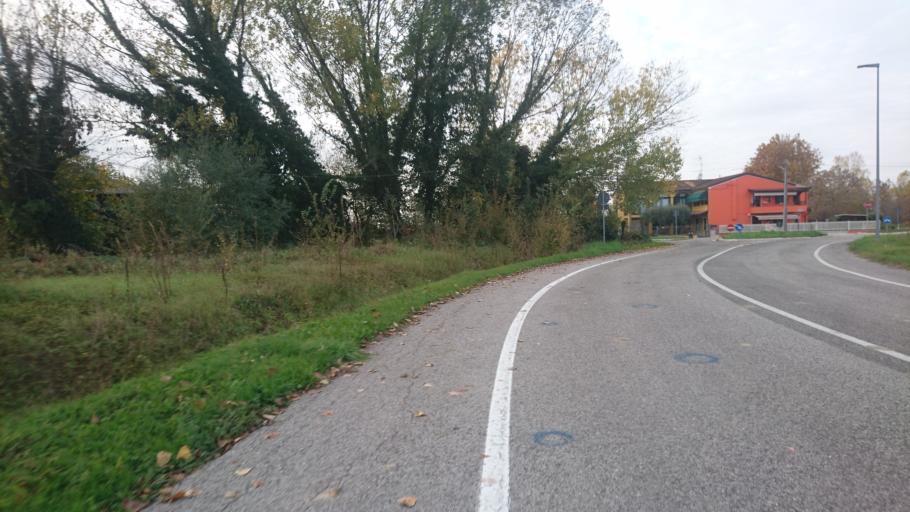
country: IT
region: Veneto
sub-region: Provincia di Padova
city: Tencarola
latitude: 45.3802
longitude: 11.8241
